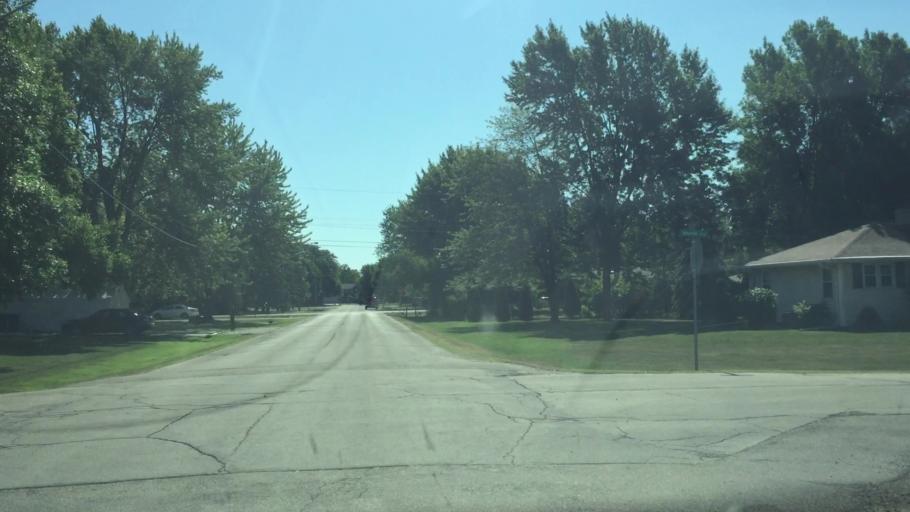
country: US
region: Wisconsin
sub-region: Winnebago County
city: Menasha
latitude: 44.2187
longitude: -88.4136
